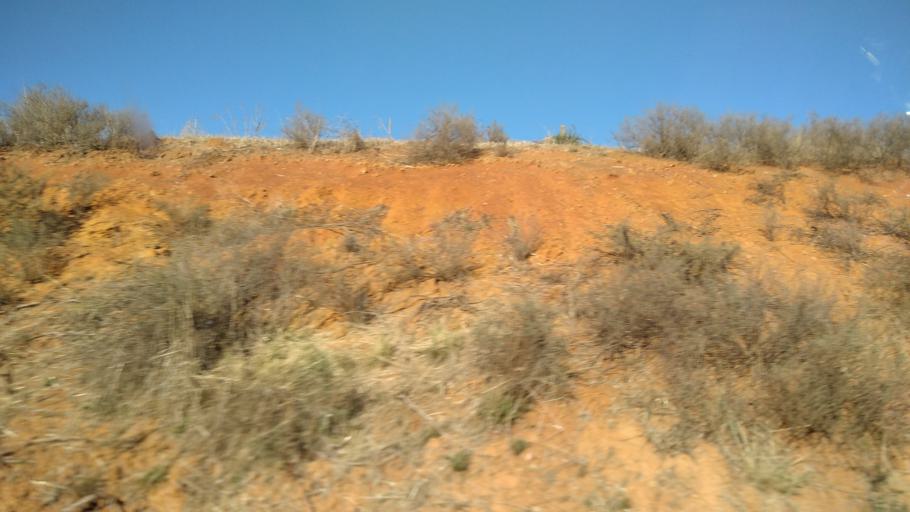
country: ZA
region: Western Cape
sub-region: West Coast District Municipality
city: Malmesbury
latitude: -33.4003
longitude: 18.6906
